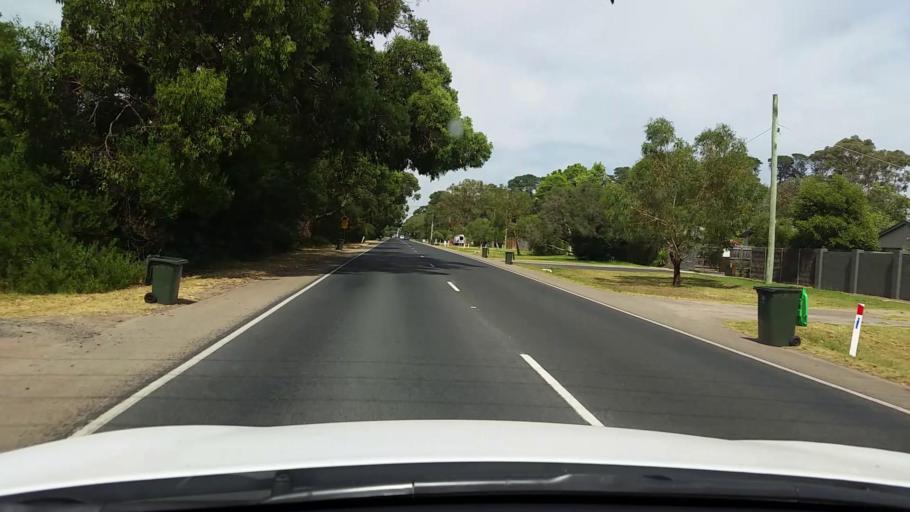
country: AU
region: Victoria
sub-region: Mornington Peninsula
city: Crib Point
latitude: -38.3435
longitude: 145.1697
